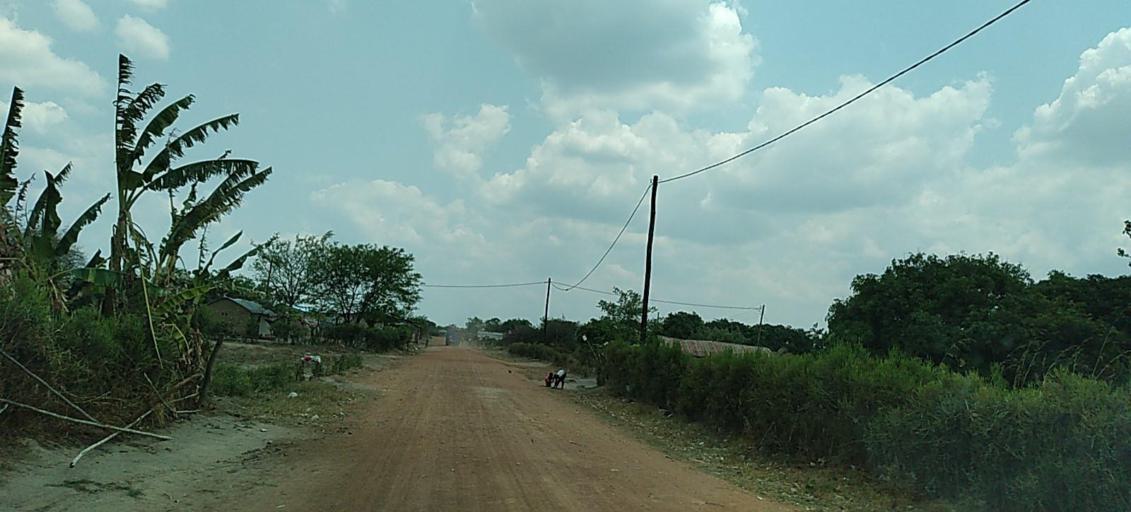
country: ZM
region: Copperbelt
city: Luanshya
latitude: -13.1240
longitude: 28.3102
